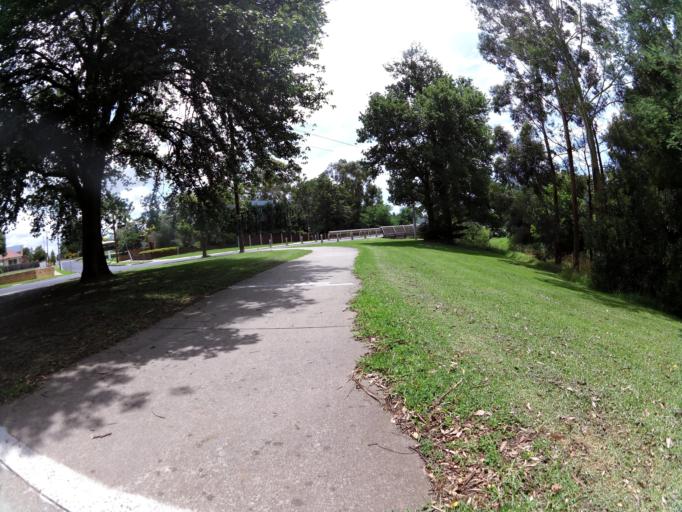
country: AU
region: Victoria
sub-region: Latrobe
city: Traralgon
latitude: -38.1916
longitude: 146.5389
